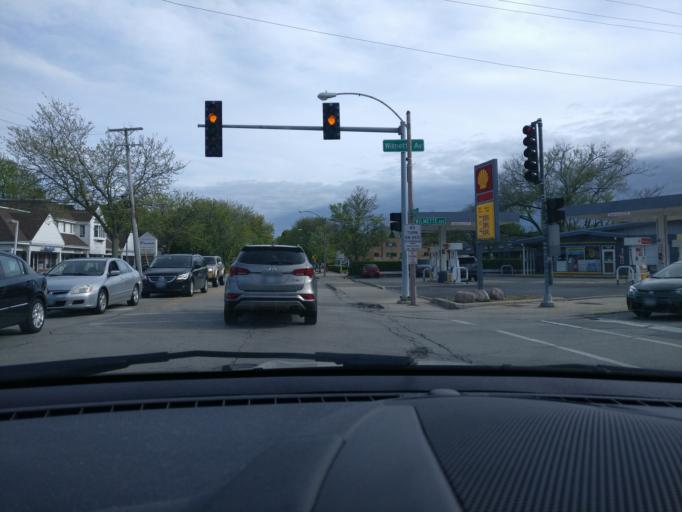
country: US
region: Illinois
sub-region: Cook County
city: Wilmette
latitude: 42.0723
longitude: -87.7227
